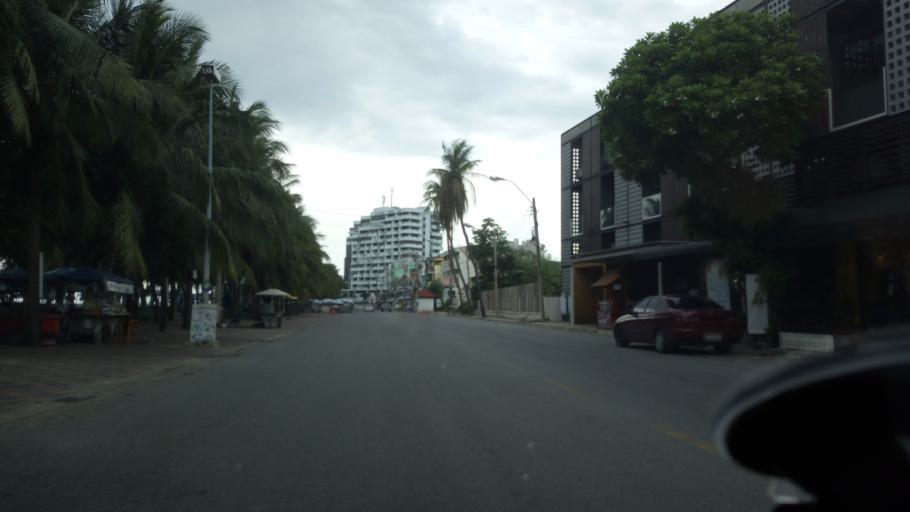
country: TH
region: Chon Buri
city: Chon Buri
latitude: 13.2988
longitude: 100.9018
